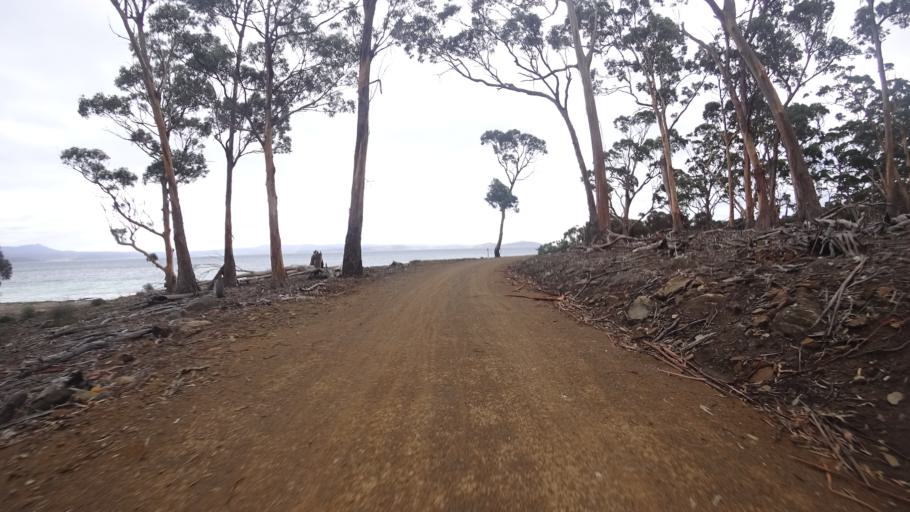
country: AU
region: Tasmania
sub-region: Sorell
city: Sorell
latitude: -42.6100
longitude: 148.0467
